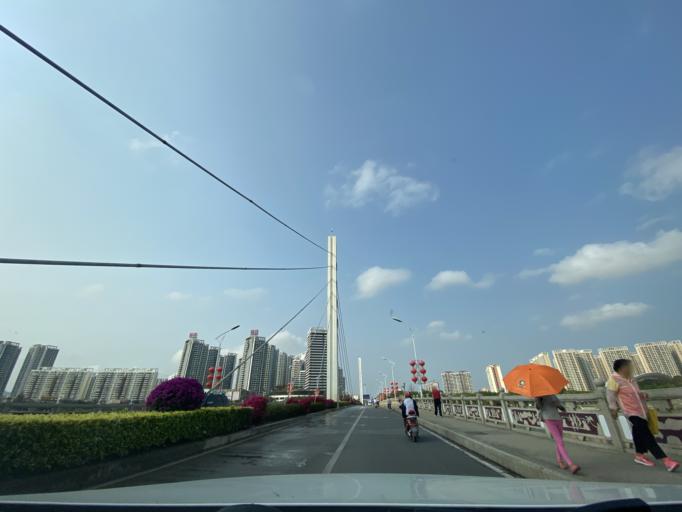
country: CN
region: Hainan
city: Yelin
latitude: 18.5174
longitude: 110.0313
